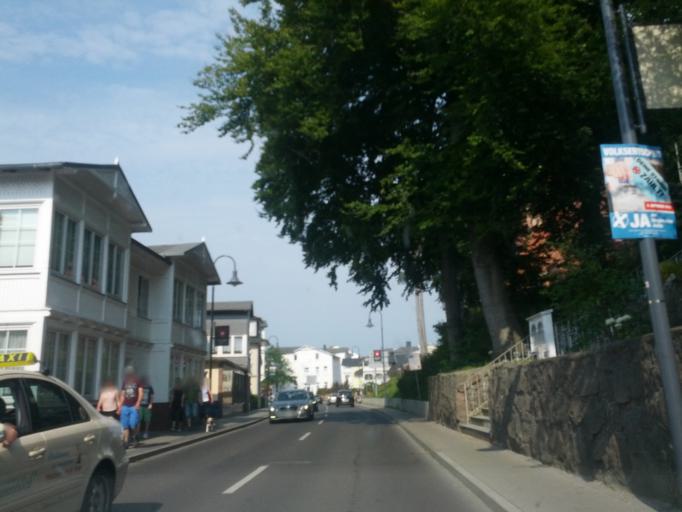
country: DE
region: Mecklenburg-Vorpommern
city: Ostseebad Binz
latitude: 54.3981
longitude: 13.6091
